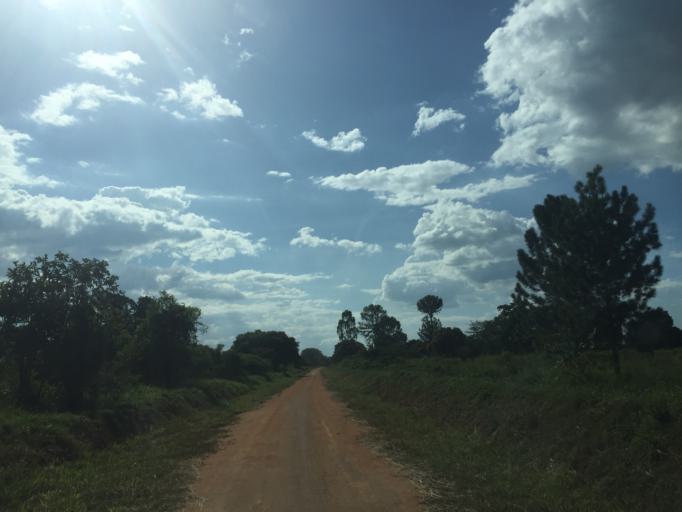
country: UG
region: Western Region
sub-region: Kiryandongo District
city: Masindi Port
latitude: 1.5280
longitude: 32.0963
